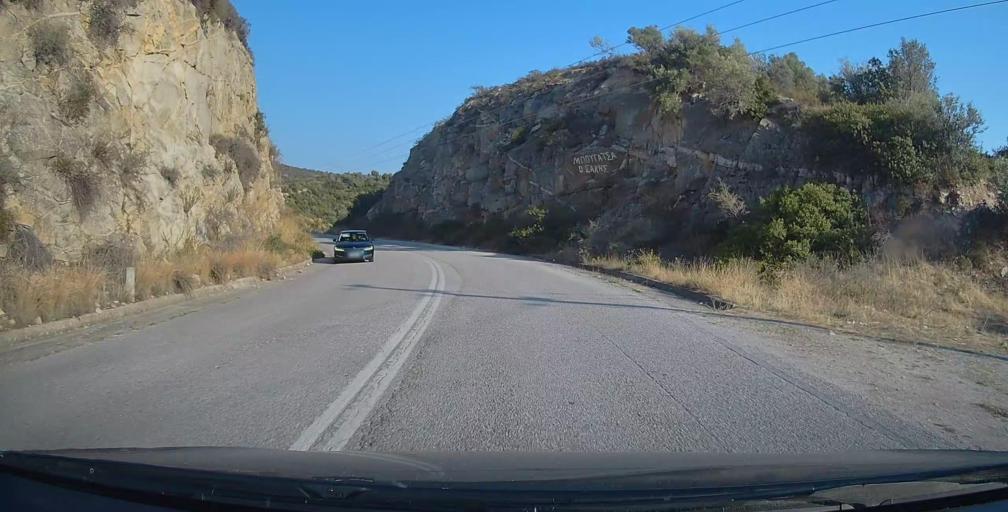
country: GR
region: Central Macedonia
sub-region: Nomos Chalkidikis
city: Sykia
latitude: 40.0062
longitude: 23.8800
